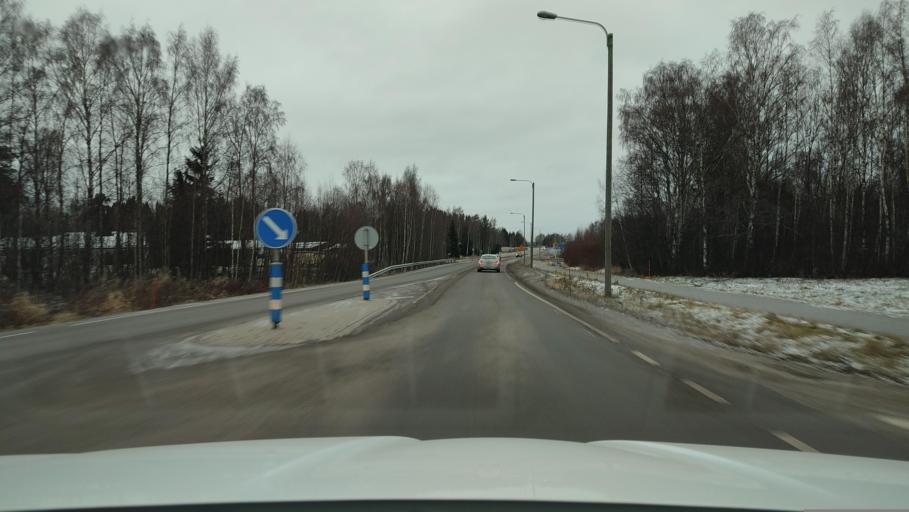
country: FI
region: Ostrobothnia
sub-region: Vaasa
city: Smedsby
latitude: 63.1223
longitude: 21.7069
